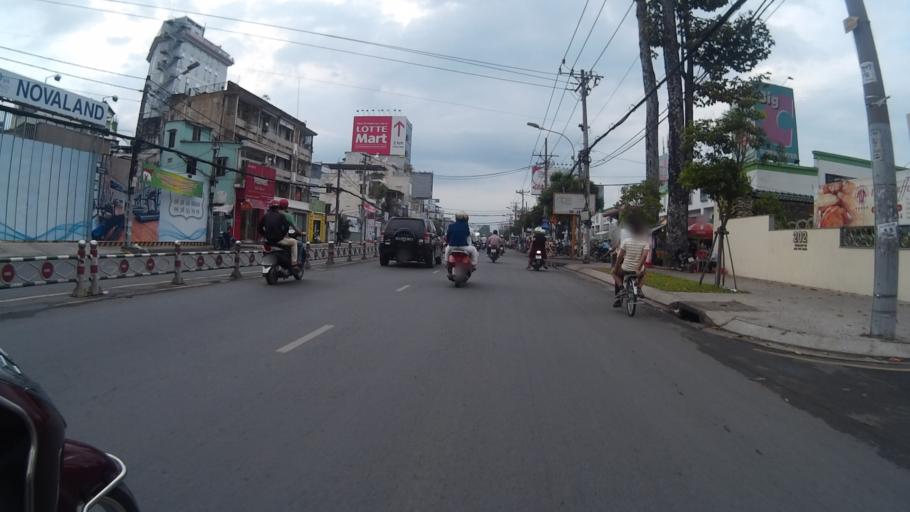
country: VN
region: Ho Chi Minh City
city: Quan Phu Nhuan
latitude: 10.8000
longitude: 106.6704
